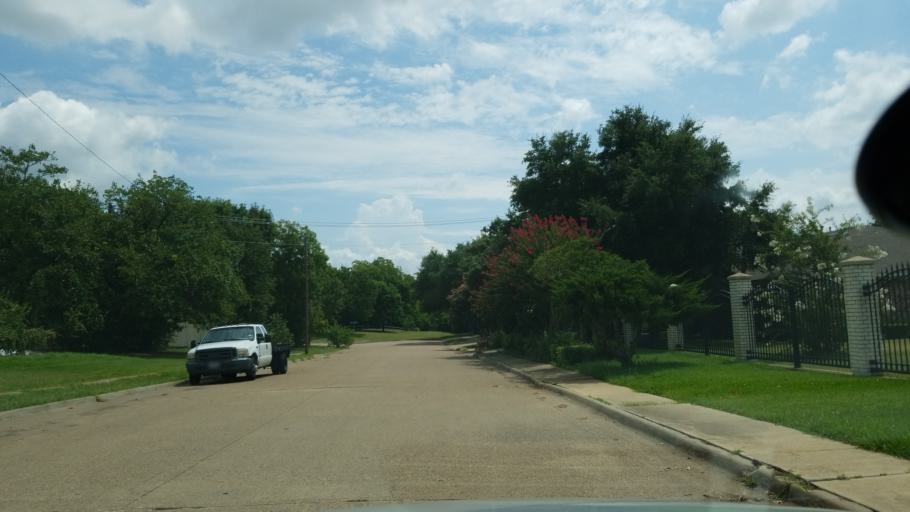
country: US
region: Texas
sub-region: Dallas County
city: Garland
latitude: 32.9152
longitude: -96.6621
